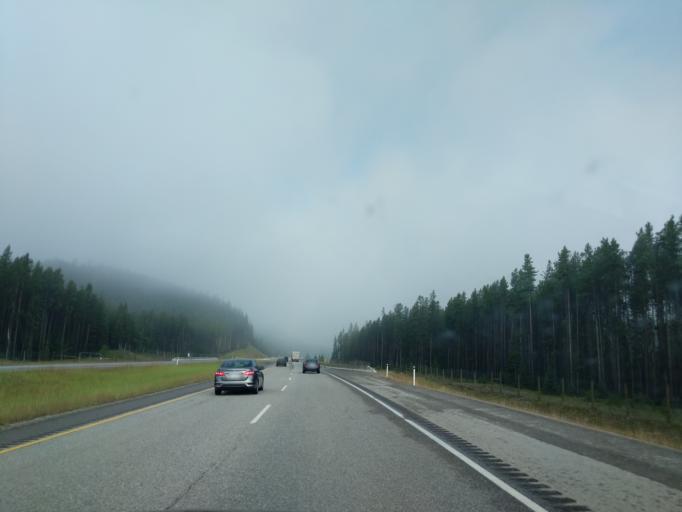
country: CA
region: Alberta
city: Lake Louise
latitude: 51.2838
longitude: -115.9787
